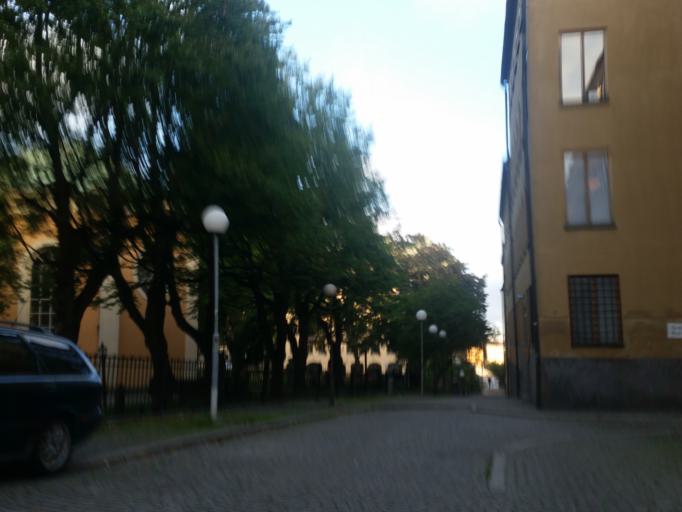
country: SE
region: Stockholm
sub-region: Stockholms Kommun
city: Stockholm
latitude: 59.3185
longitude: 18.0683
